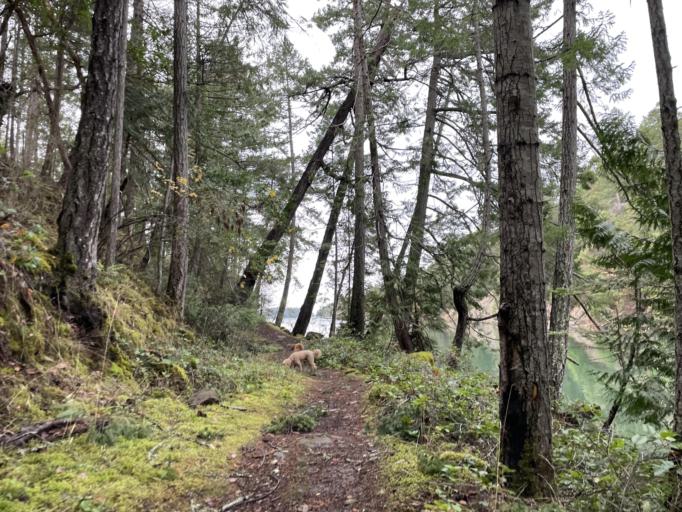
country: CA
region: British Columbia
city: North Cowichan
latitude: 48.9402
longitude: -123.5510
